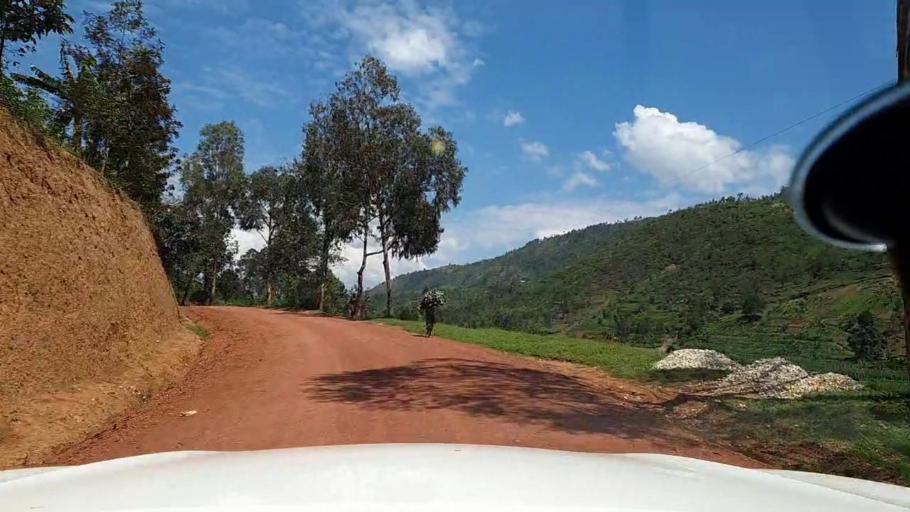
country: RW
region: Kigali
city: Kigali
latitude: -1.7889
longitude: 29.8834
